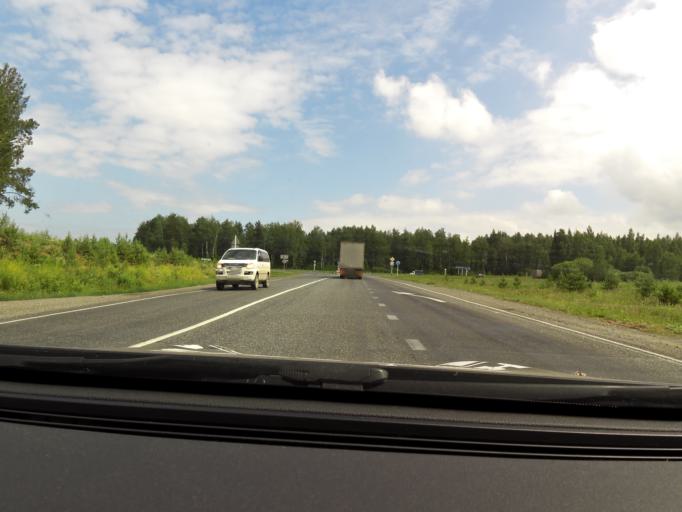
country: RU
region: Perm
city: Suksun
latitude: 57.0924
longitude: 57.3891
